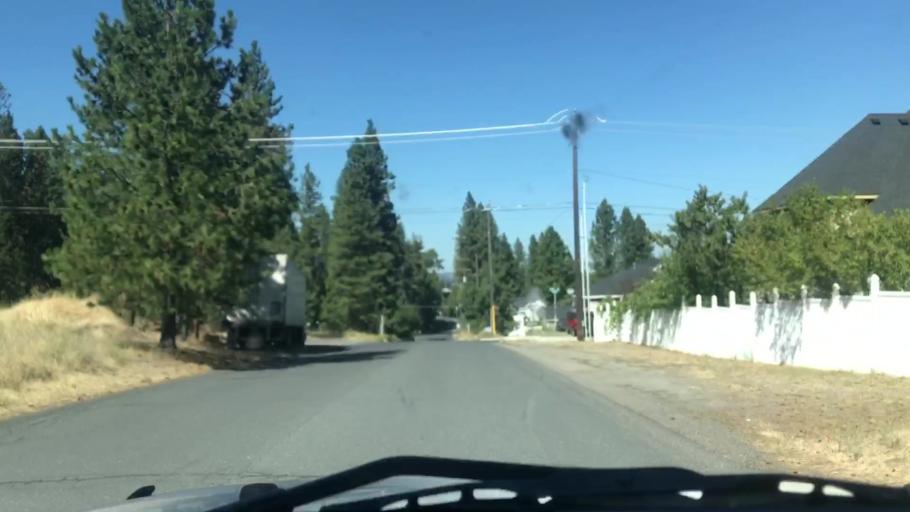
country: US
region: Washington
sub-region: Spokane County
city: Spokane
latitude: 47.6414
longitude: -117.4516
